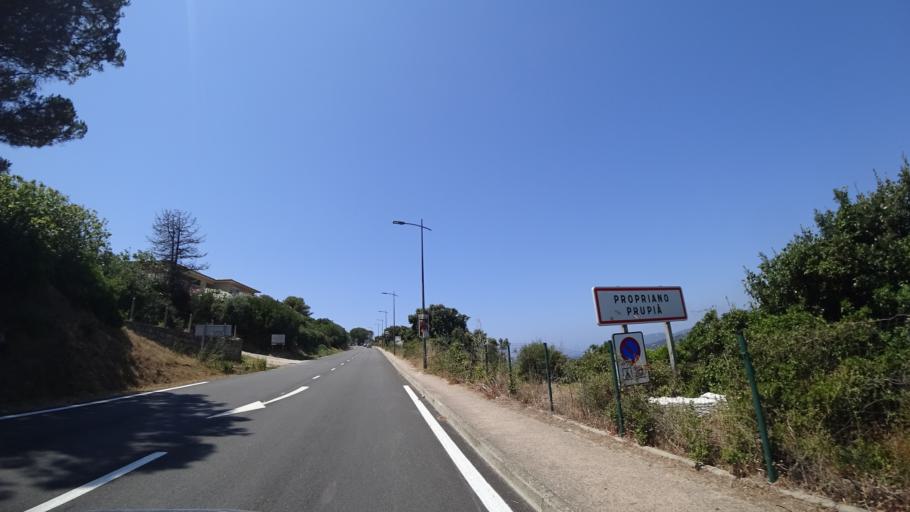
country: FR
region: Corsica
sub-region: Departement de la Corse-du-Sud
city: Propriano
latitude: 41.6822
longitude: 8.9190
